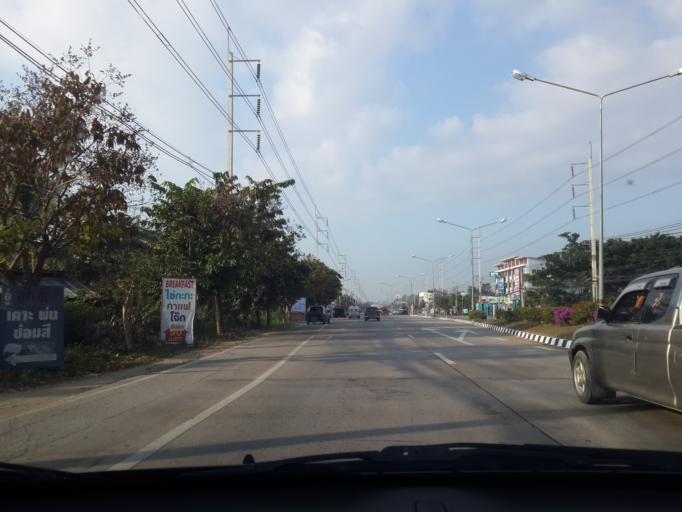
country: TH
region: Chiang Mai
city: San Sai
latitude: 18.8375
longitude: 99.0642
